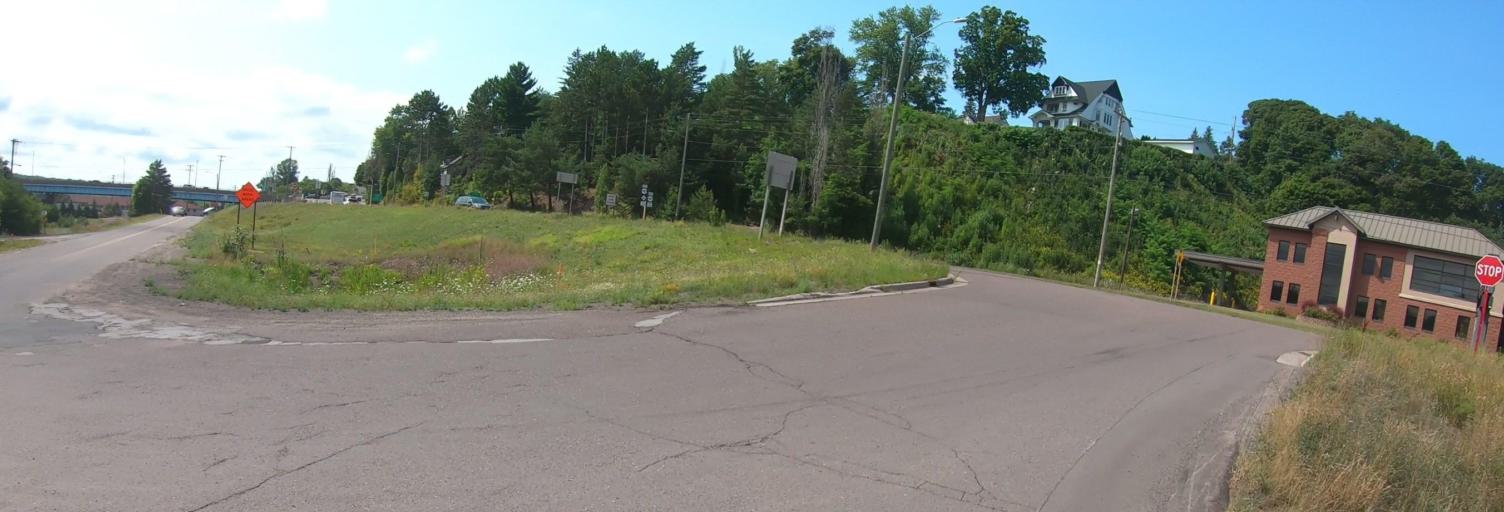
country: US
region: Michigan
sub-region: Houghton County
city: Houghton
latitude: 47.1259
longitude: -88.5712
